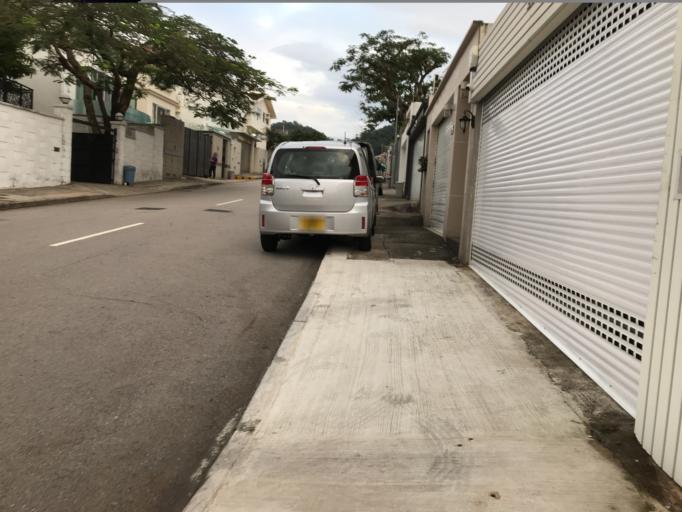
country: HK
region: Tai Po
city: Tai Po
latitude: 22.4608
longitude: 114.1534
